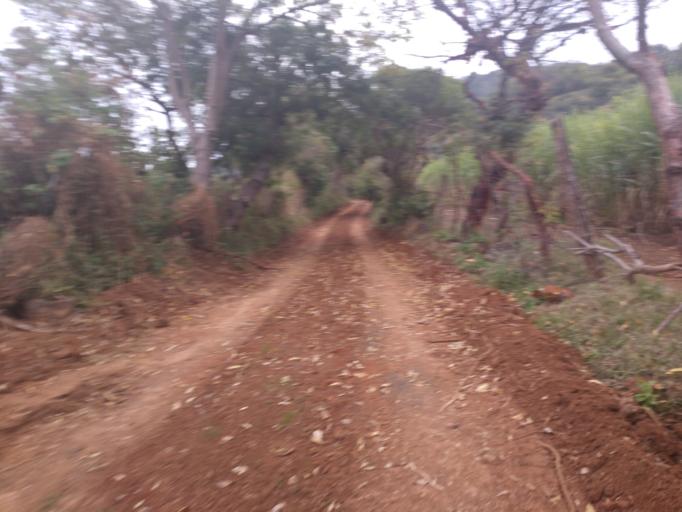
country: MX
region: Nayarit
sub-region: Tepic
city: La Corregidora
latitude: 21.4694
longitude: -104.7894
